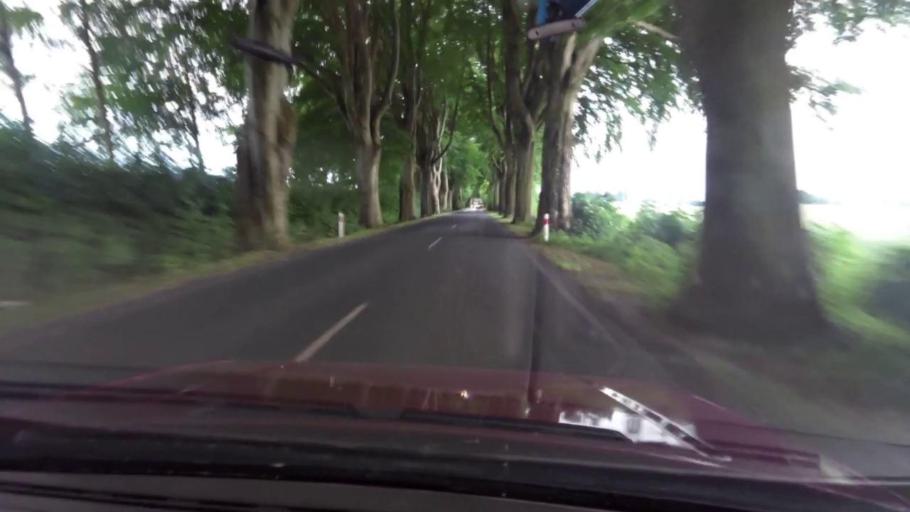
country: PL
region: West Pomeranian Voivodeship
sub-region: Powiat koszalinski
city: Polanow
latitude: 54.1403
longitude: 16.5525
